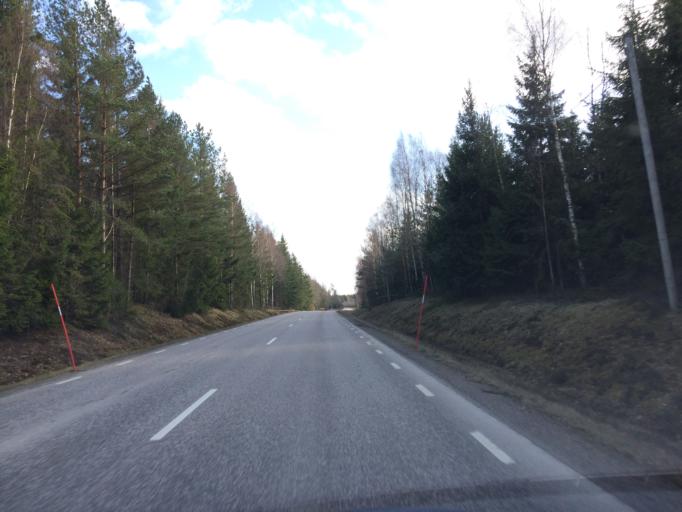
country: SE
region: Kronoberg
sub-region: Almhults Kommun
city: AElmhult
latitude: 56.5883
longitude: 14.0979
